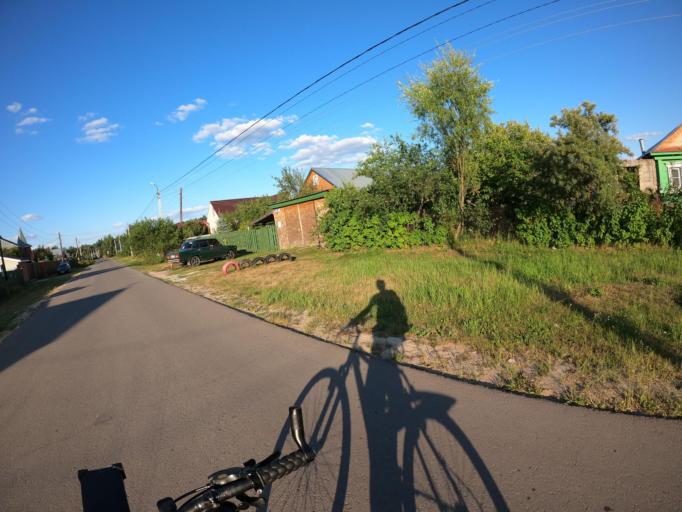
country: RU
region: Moskovskaya
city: Beloozerskiy
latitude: 55.4921
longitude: 38.4357
